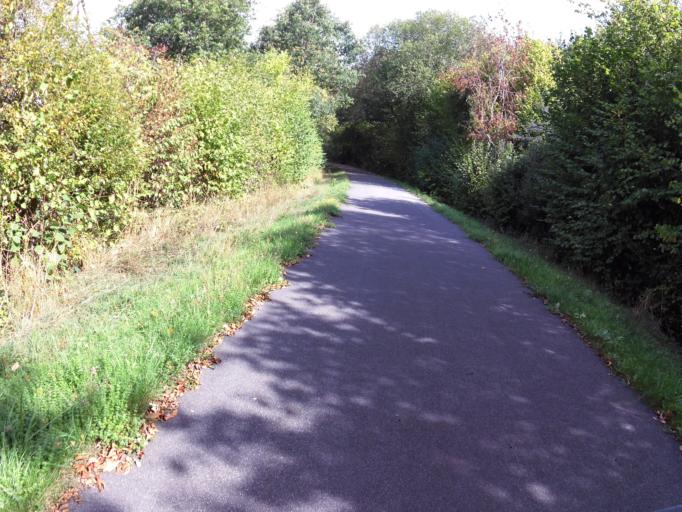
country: DE
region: Rheinland-Pfalz
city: Kickeshausen
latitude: 50.0671
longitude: 6.2532
